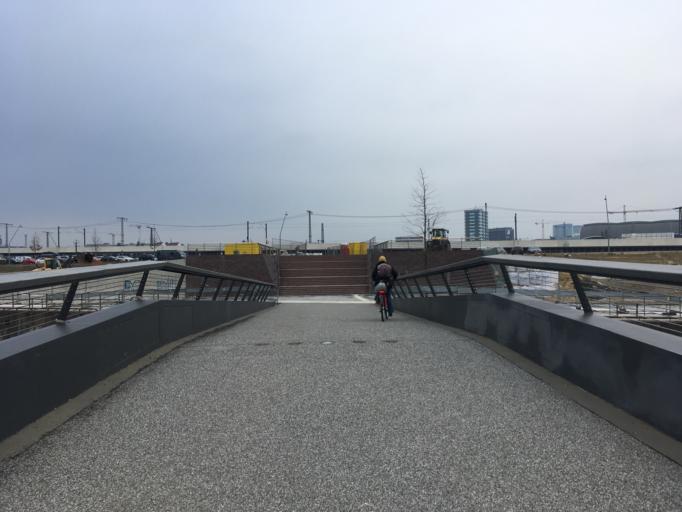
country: DE
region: Hamburg
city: Hamburg-Mitte
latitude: 53.5388
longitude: 10.0137
